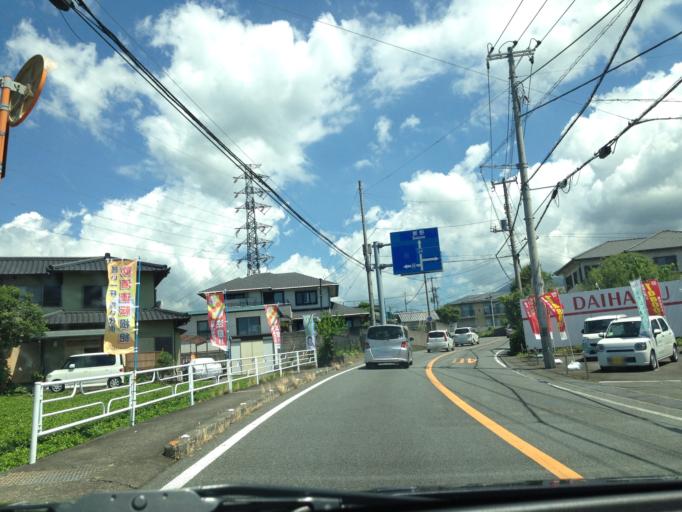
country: JP
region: Shizuoka
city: Fuji
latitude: 35.1859
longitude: 138.7033
